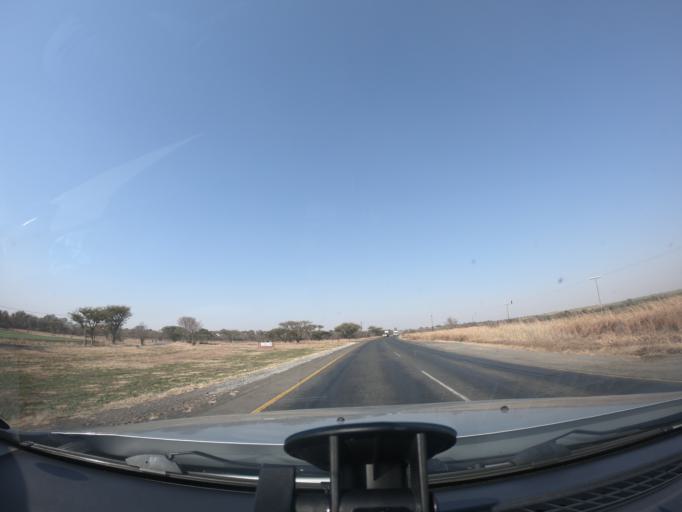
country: ZA
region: KwaZulu-Natal
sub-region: uThukela District Municipality
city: Ladysmith
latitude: -28.7368
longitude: 29.8168
